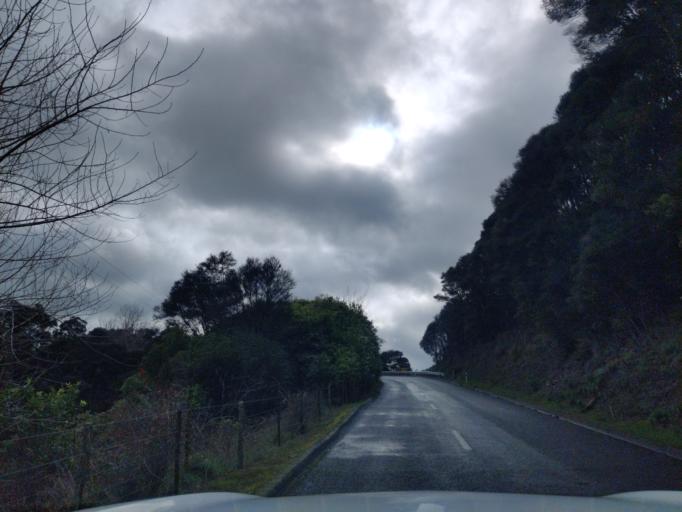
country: NZ
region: Manawatu-Wanganui
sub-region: Palmerston North City
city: Palmerston North
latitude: -40.1944
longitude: 175.7818
